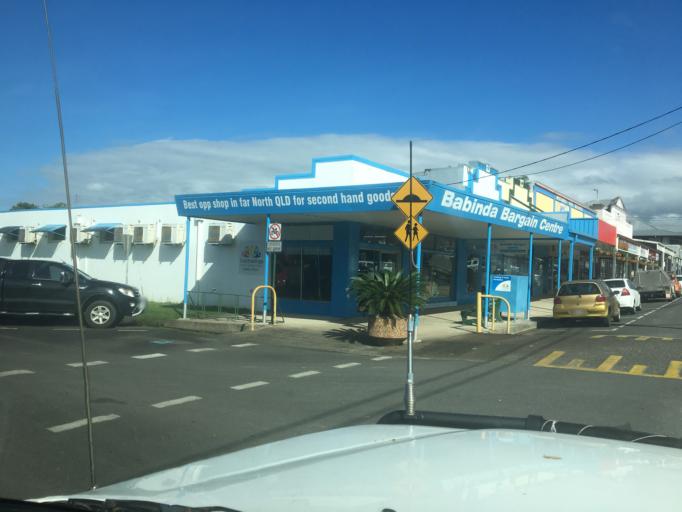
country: AU
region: Queensland
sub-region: Cassowary Coast
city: Innisfail
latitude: -17.3442
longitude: 145.9235
